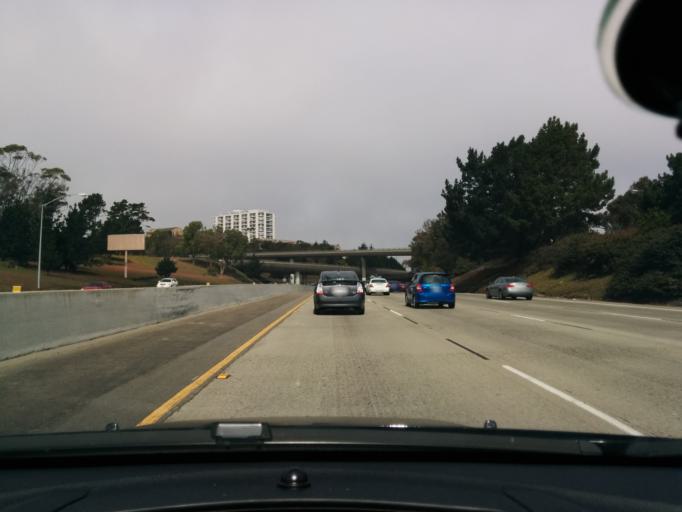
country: US
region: California
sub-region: San Mateo County
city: Colma
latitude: 37.6757
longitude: -122.4698
